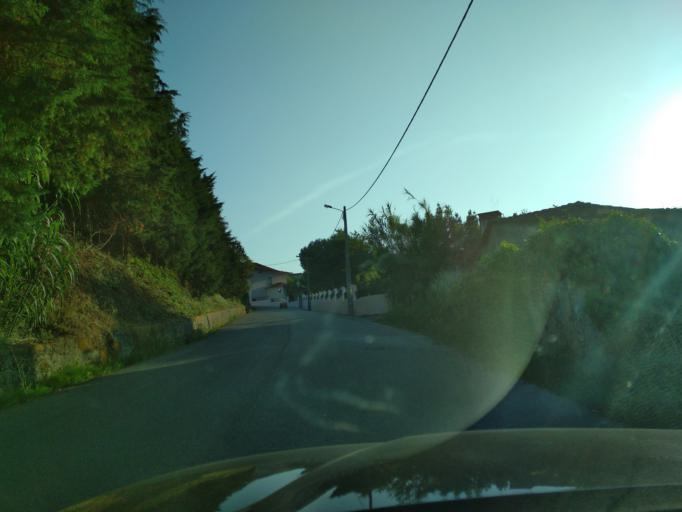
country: PT
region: Coimbra
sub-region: Coimbra
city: Coimbra
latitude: 40.2683
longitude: -8.4500
